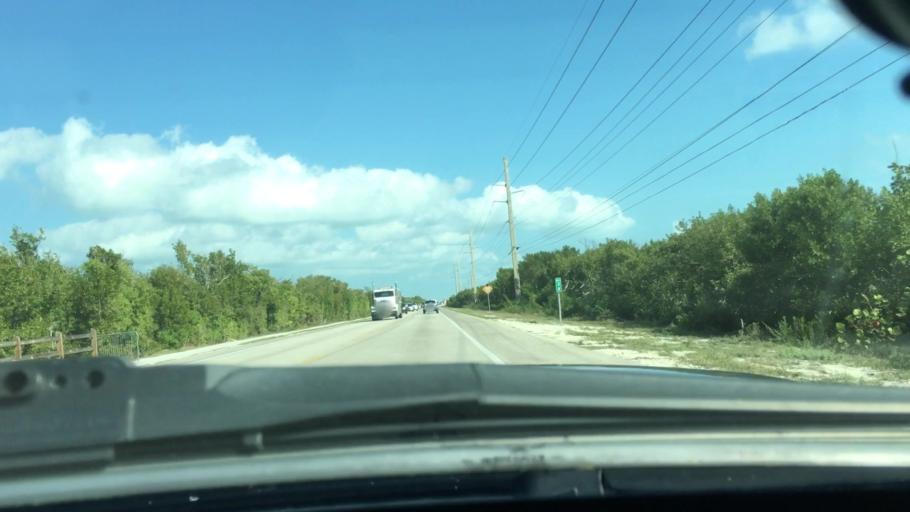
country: US
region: Florida
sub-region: Monroe County
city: Big Pine Key
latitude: 24.6671
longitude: -81.2576
